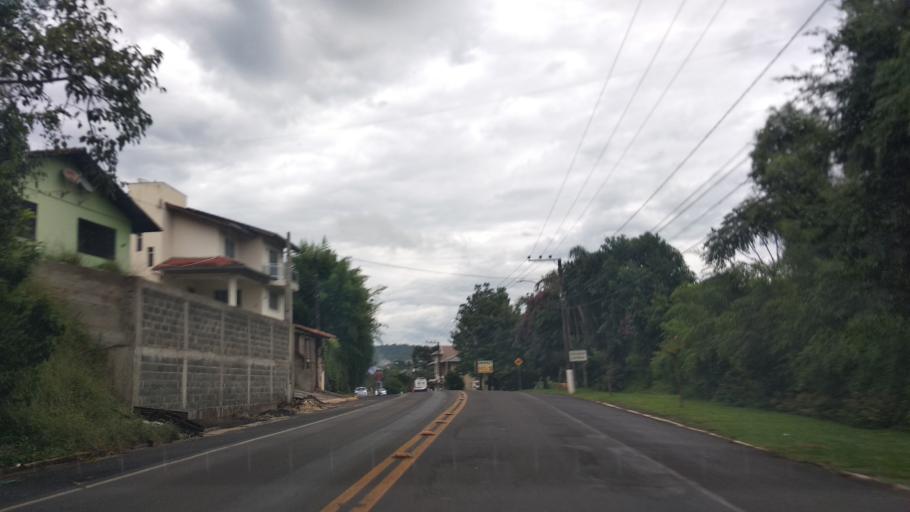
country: BR
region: Santa Catarina
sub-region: Videira
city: Videira
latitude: -27.0971
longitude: -51.2488
